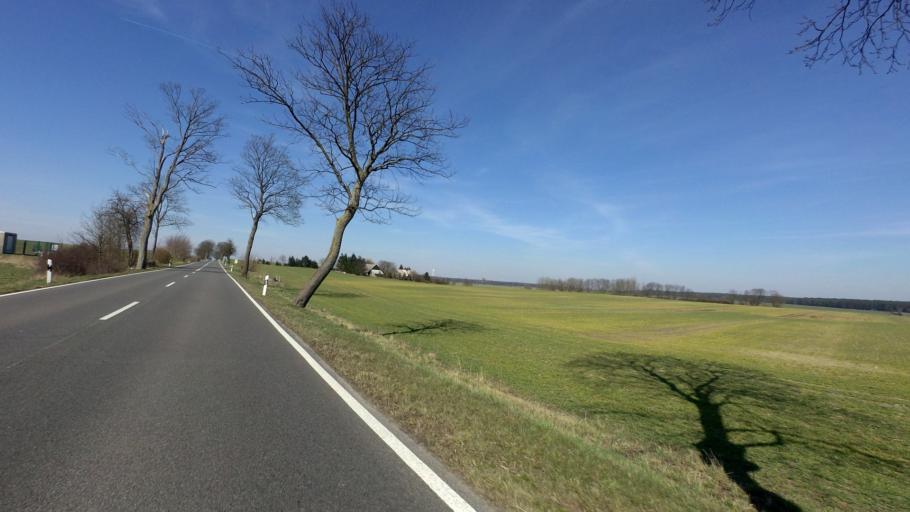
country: DE
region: Brandenburg
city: Protzel
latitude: 52.6128
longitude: 14.0206
